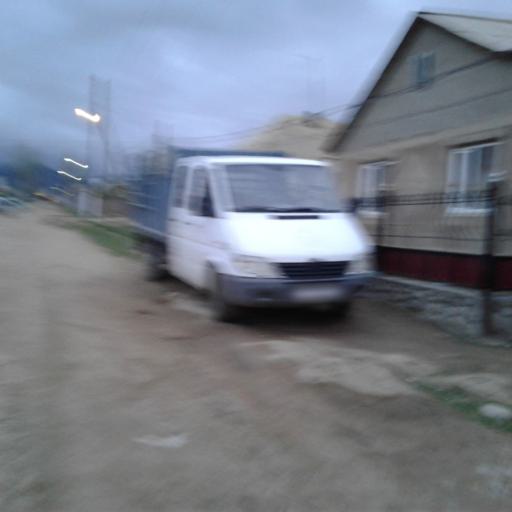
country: KG
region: Ysyk-Koel
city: Bokombayevskoye
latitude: 42.1109
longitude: 76.9864
